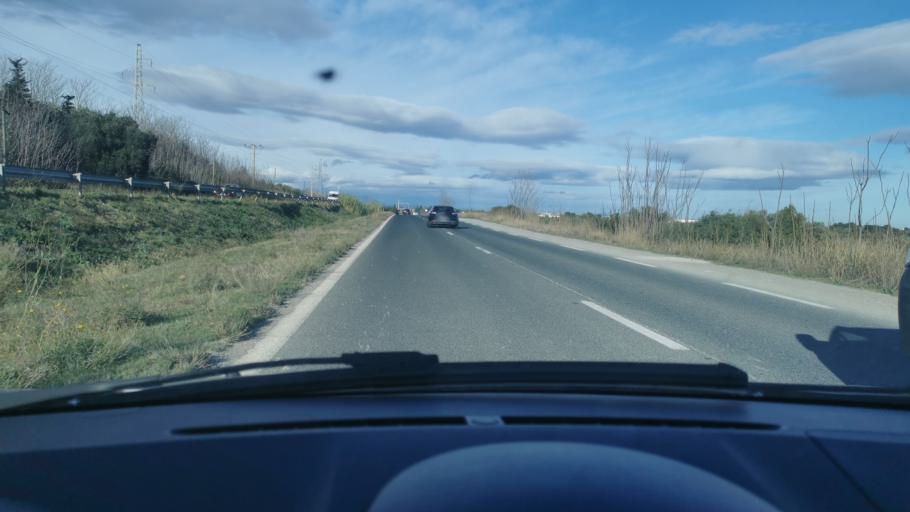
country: FR
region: Languedoc-Roussillon
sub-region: Departement de l'Herault
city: Mireval
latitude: 43.5342
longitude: 3.8228
